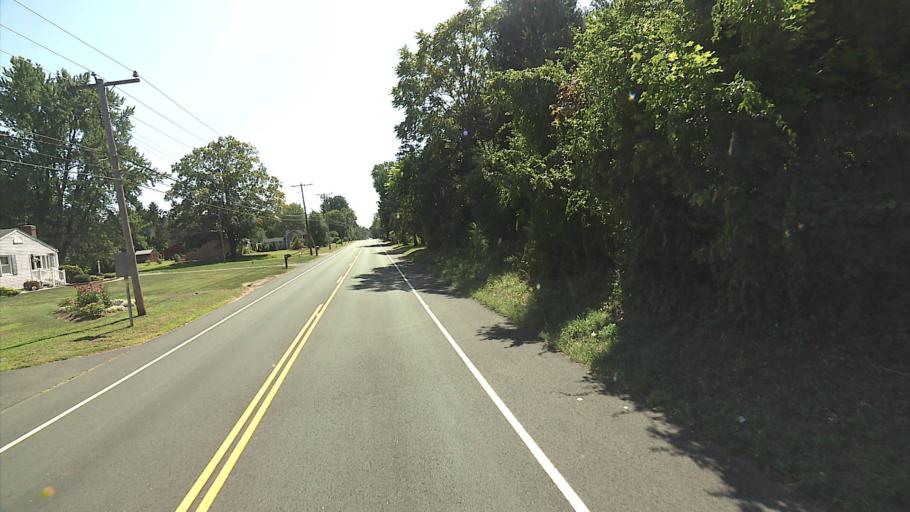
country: US
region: Connecticut
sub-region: Hartford County
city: Windsor Locks
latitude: 41.9004
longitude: -72.6256
